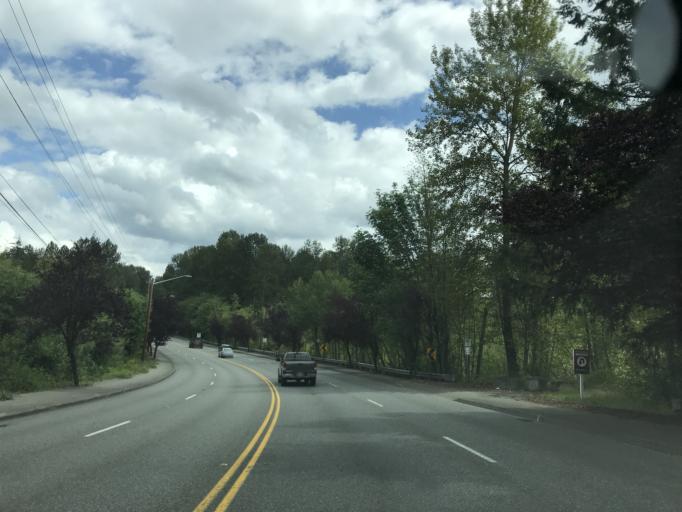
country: US
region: Washington
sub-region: King County
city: Fairwood
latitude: 47.4456
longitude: -122.1672
